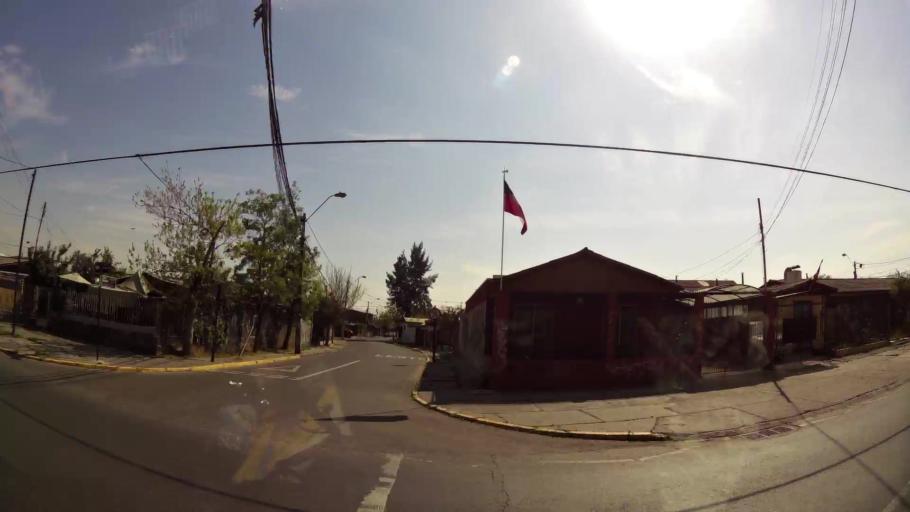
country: CL
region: Santiago Metropolitan
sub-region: Provincia de Maipo
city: San Bernardo
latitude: -33.5542
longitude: -70.6720
